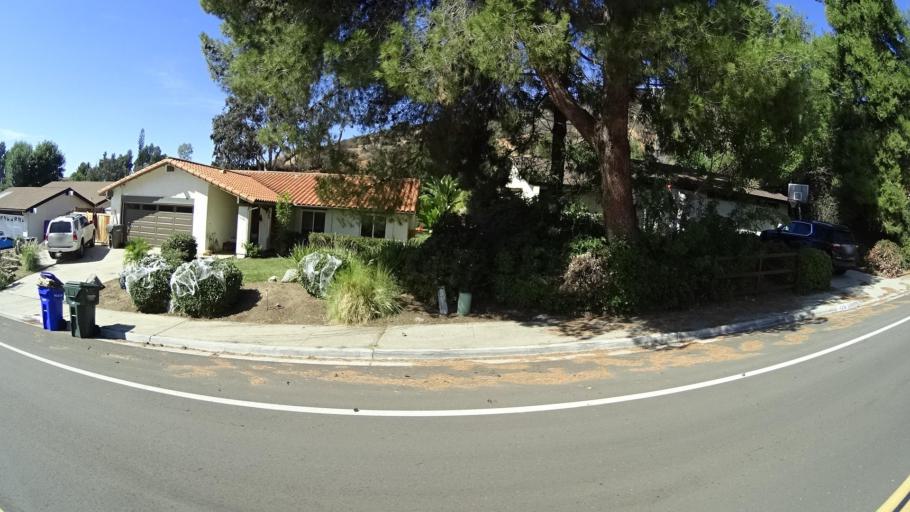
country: US
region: California
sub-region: San Diego County
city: Casa de Oro-Mount Helix
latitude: 32.7538
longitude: -116.9733
